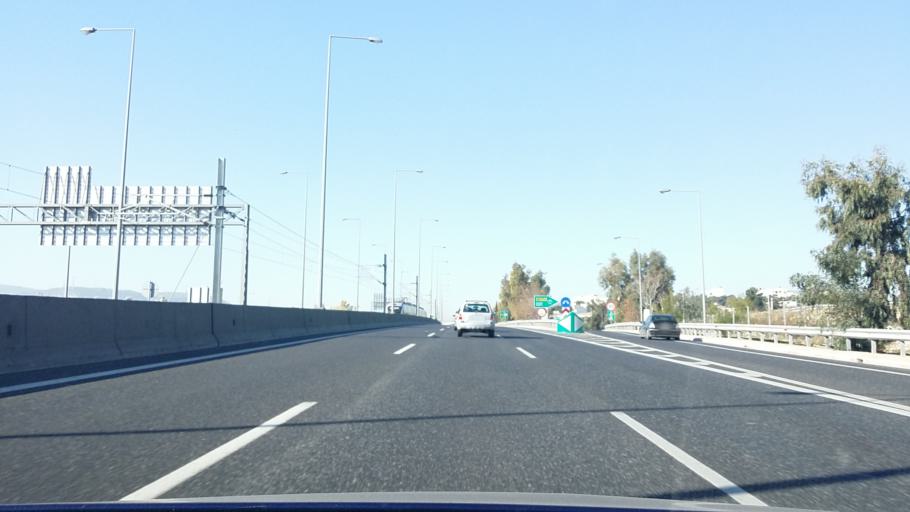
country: GR
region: Attica
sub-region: Nomarchia Anatolikis Attikis
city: Acharnes
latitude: 38.0662
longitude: 23.7363
